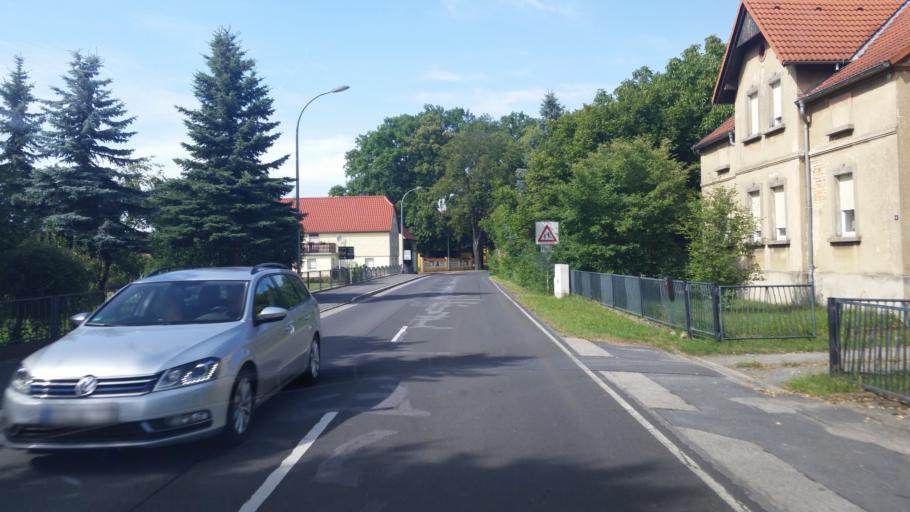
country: DE
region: Saxony
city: Bernsdorf
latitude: 51.3508
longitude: 14.0652
